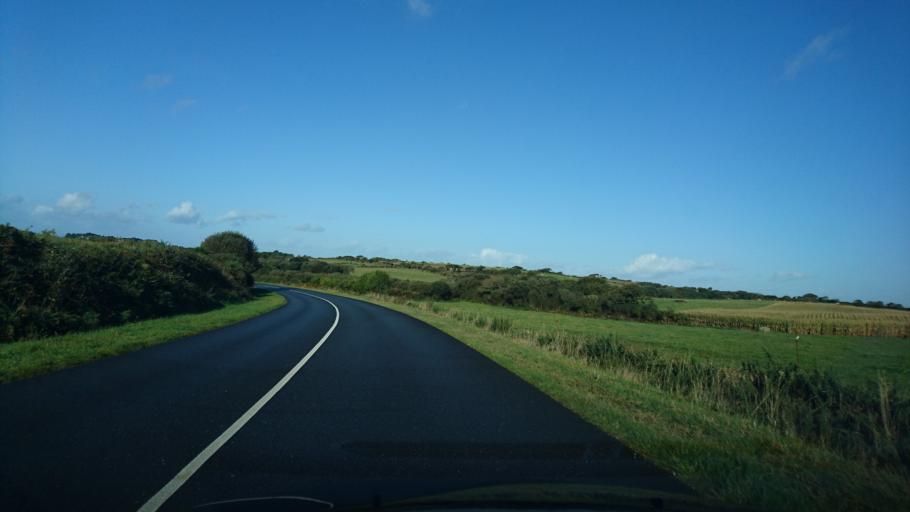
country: FR
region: Brittany
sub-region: Departement du Finistere
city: Plouarzel
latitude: 48.4381
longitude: -4.7174
